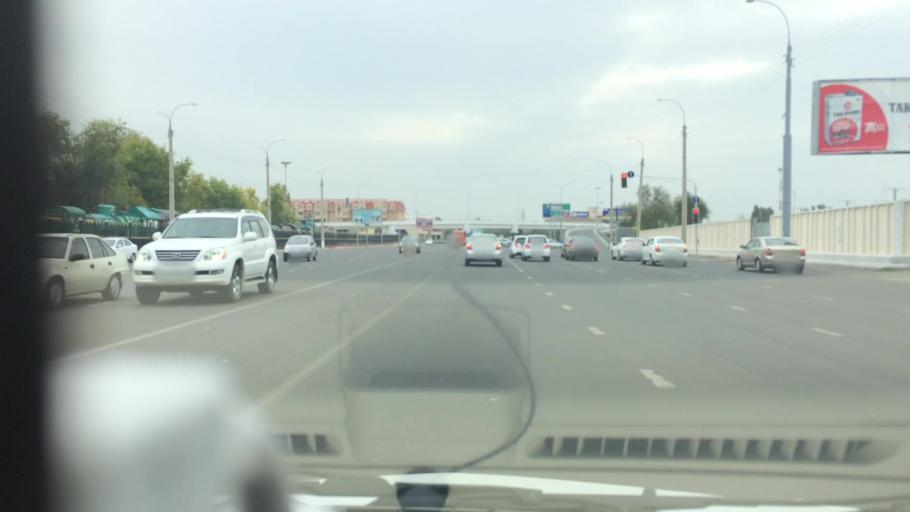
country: UZ
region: Toshkent Shahri
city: Tashkent
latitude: 41.2947
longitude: 69.2906
